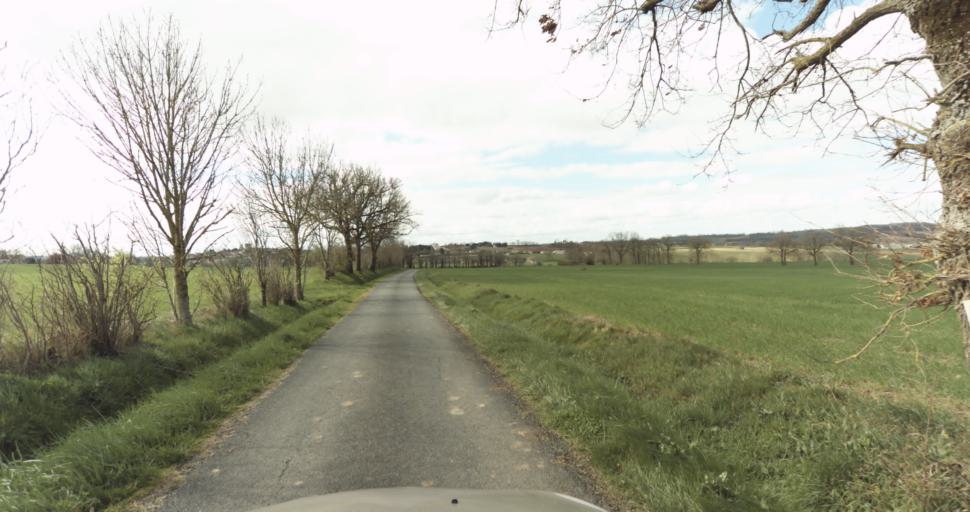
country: FR
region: Midi-Pyrenees
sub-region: Departement du Tarn
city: Frejairolles
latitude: 43.8566
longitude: 2.2066
